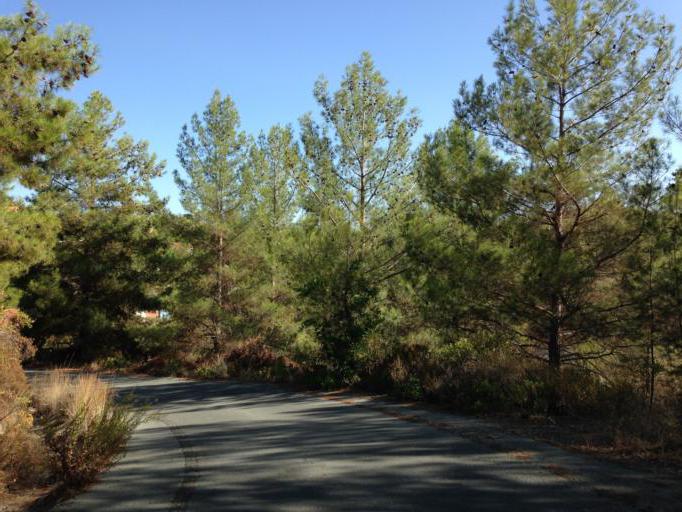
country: CY
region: Limassol
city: Pachna
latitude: 34.8877
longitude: 32.8384
